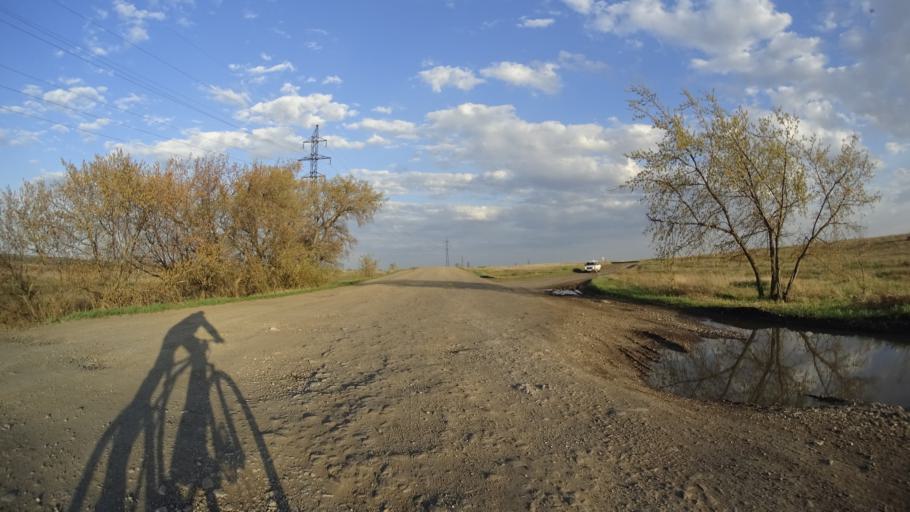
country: RU
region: Chelyabinsk
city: Troitsk
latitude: 54.0531
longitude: 61.5911
